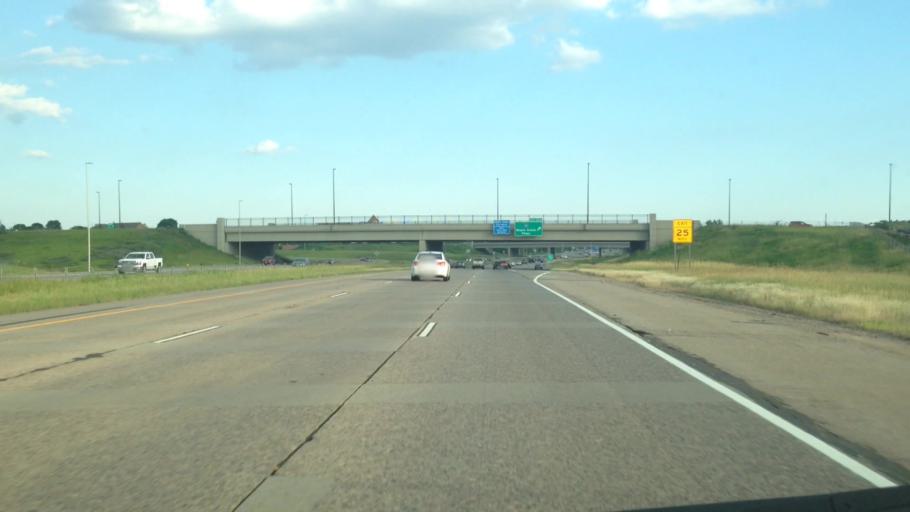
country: US
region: Minnesota
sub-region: Hennepin County
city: Maple Grove
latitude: 45.1295
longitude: -93.4875
